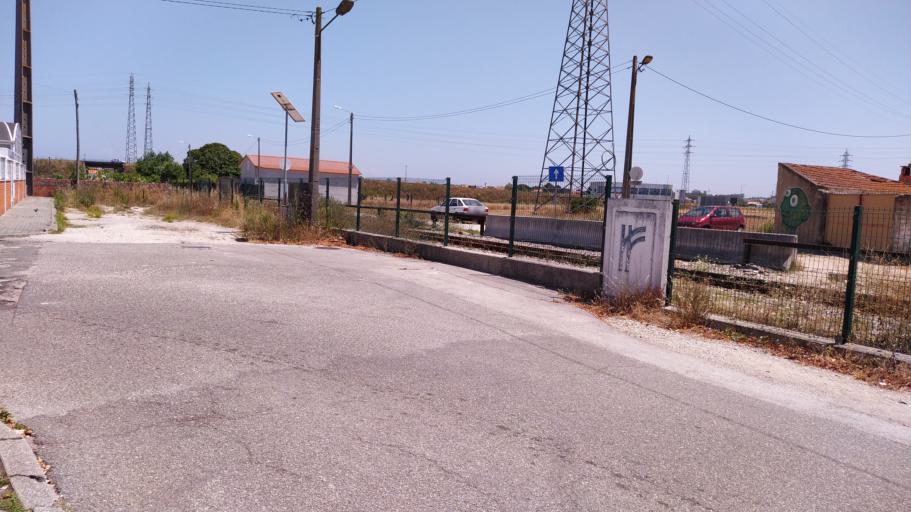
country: PT
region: Aveiro
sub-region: Aveiro
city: Aveiro
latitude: 40.6440
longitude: -8.6318
